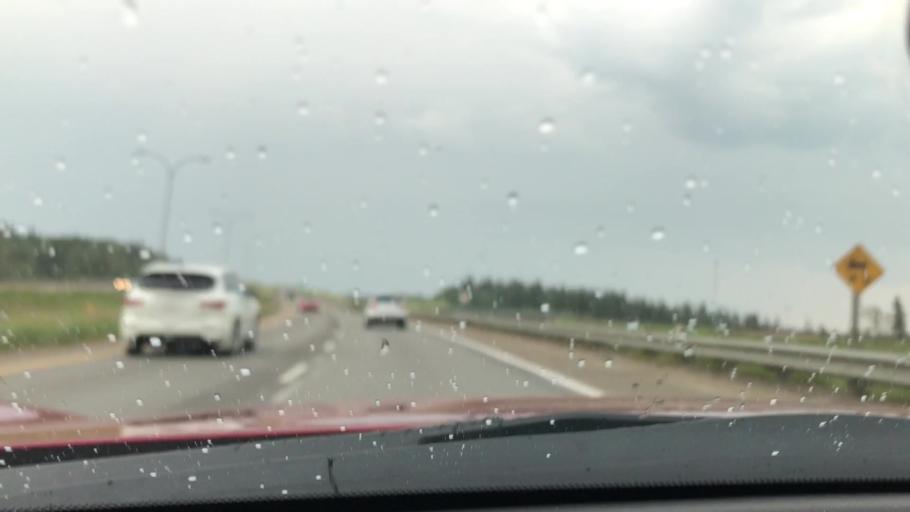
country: CA
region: Alberta
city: Red Deer
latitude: 52.2702
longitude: -113.8653
